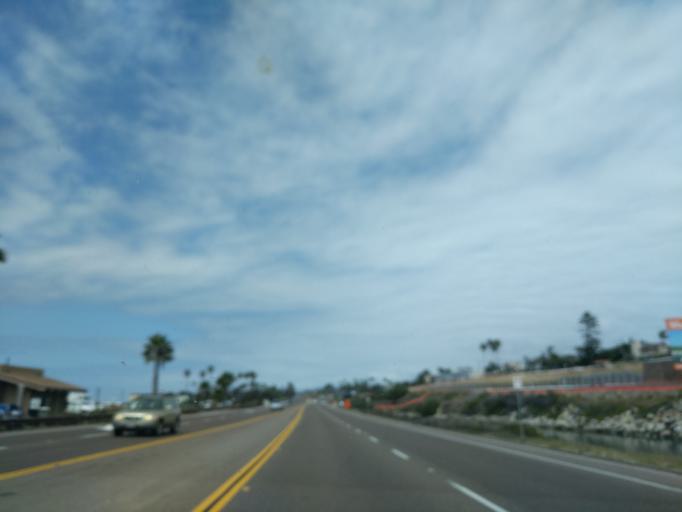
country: US
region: California
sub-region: San Diego County
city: Solana Beach
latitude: 33.0145
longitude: -117.2802
